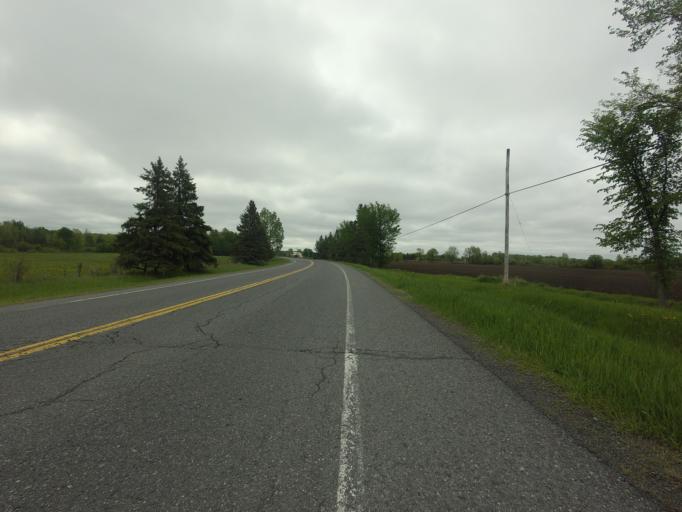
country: CA
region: Ontario
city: Casselman
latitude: 45.0511
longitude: -75.1994
